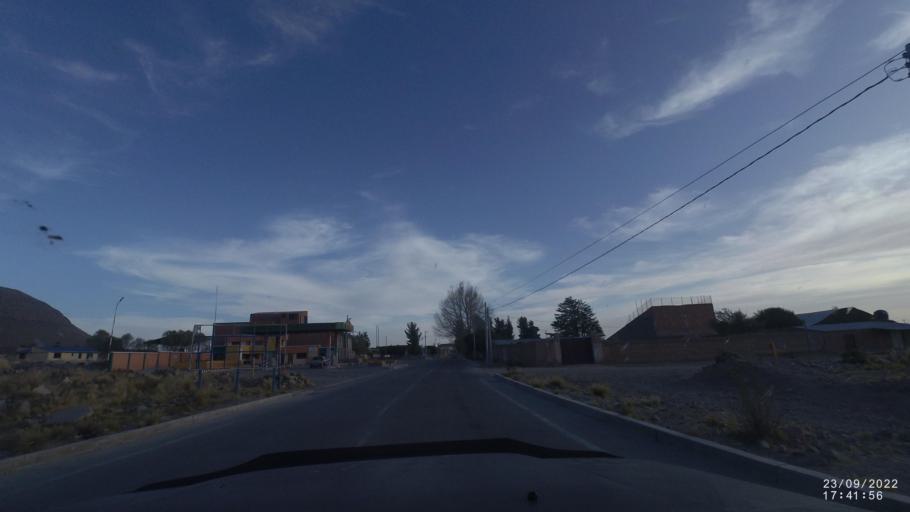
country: BO
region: Oruro
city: Challapata
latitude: -19.0070
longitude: -66.7759
